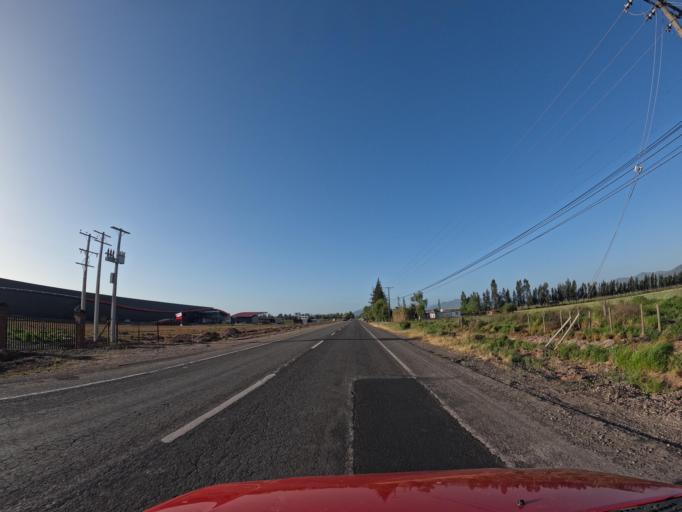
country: CL
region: O'Higgins
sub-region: Provincia de Colchagua
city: Santa Cruz
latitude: -34.5063
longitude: -71.3631
